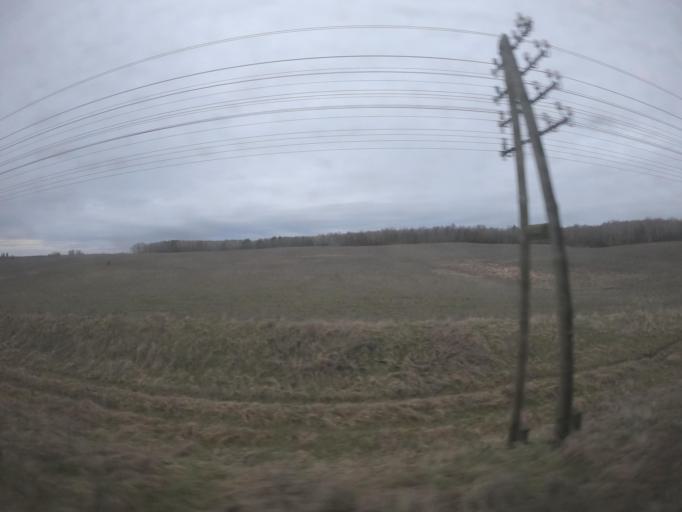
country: PL
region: West Pomeranian Voivodeship
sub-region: Powiat szczecinecki
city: Borne Sulinowo
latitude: 53.6557
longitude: 16.5804
